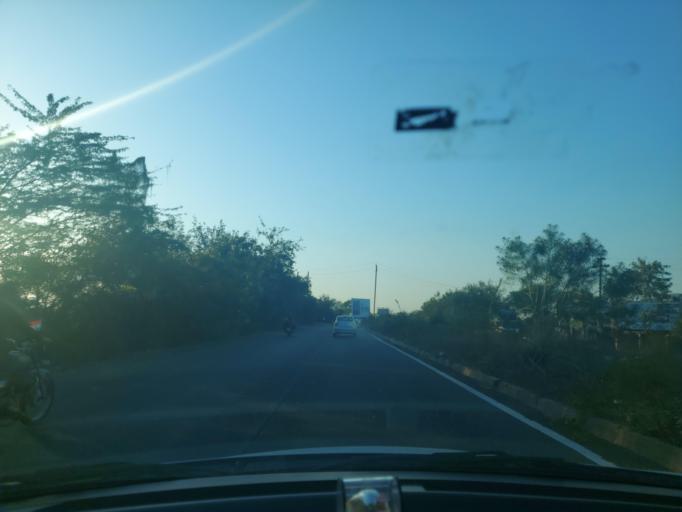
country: IN
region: Madhya Pradesh
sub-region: Ujjain
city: Ujjain
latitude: 23.0978
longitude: 75.8129
